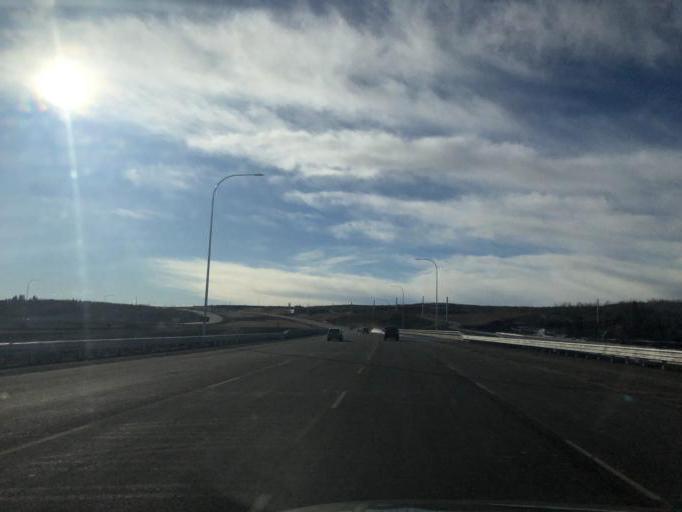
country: CA
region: Alberta
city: Calgary
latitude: 50.9943
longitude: -114.1682
